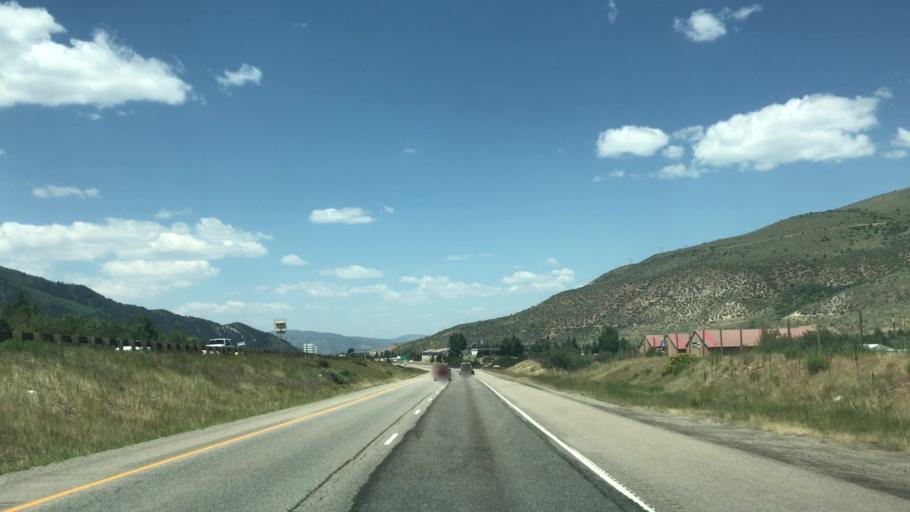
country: US
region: Colorado
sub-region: Eagle County
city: Minturn
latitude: 39.6189
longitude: -106.4664
